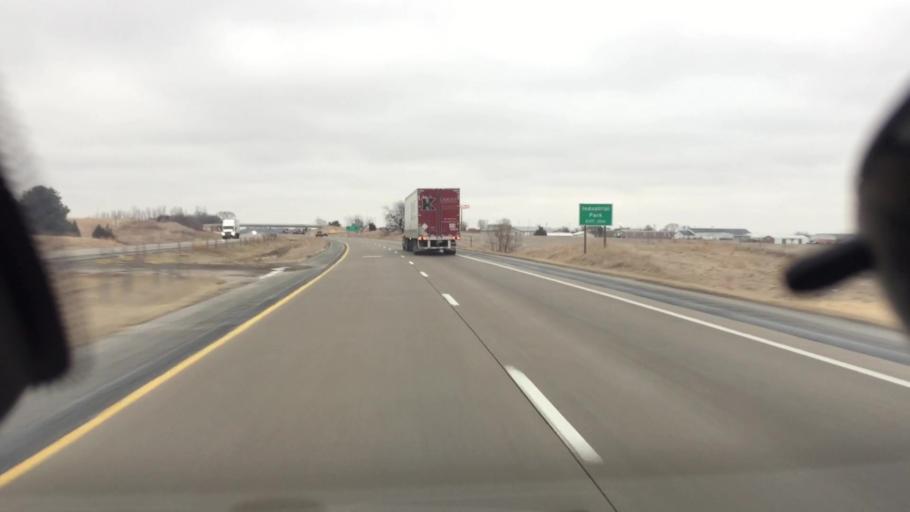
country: US
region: Iowa
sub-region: Cedar County
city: West Branch
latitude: 41.6635
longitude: -91.3563
